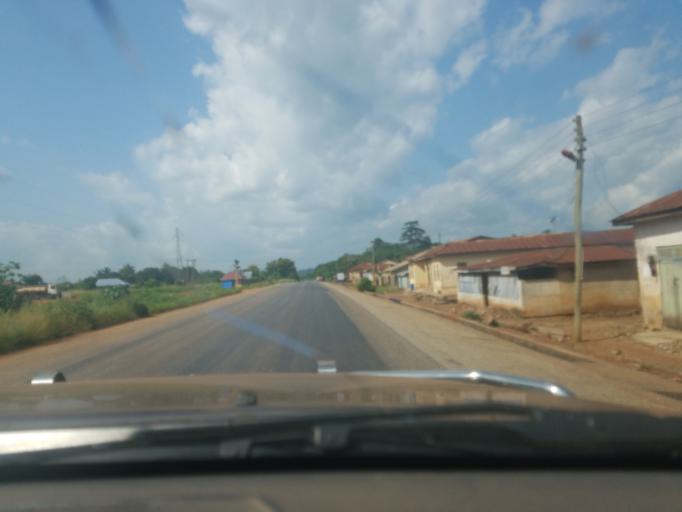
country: GH
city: Duayaw Nkwanta
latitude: 6.8835
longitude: -2.4196
